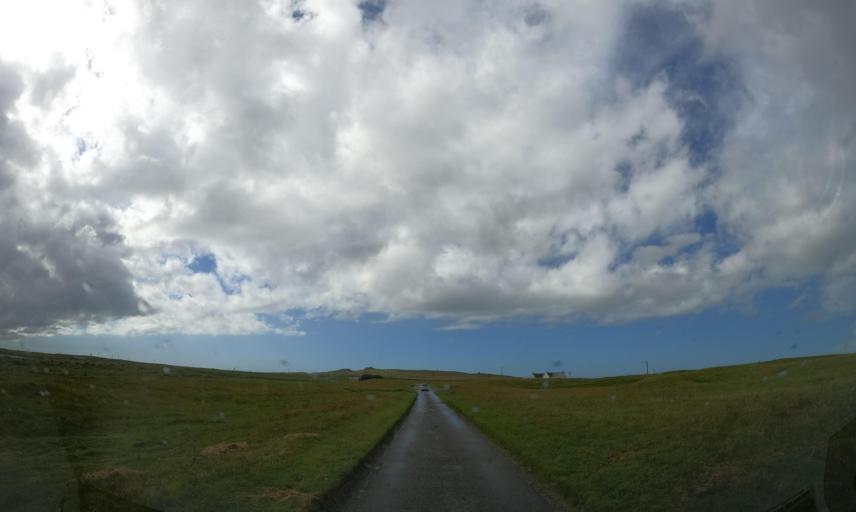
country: GB
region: Scotland
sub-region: Eilean Siar
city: Barra
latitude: 56.5156
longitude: -6.8151
